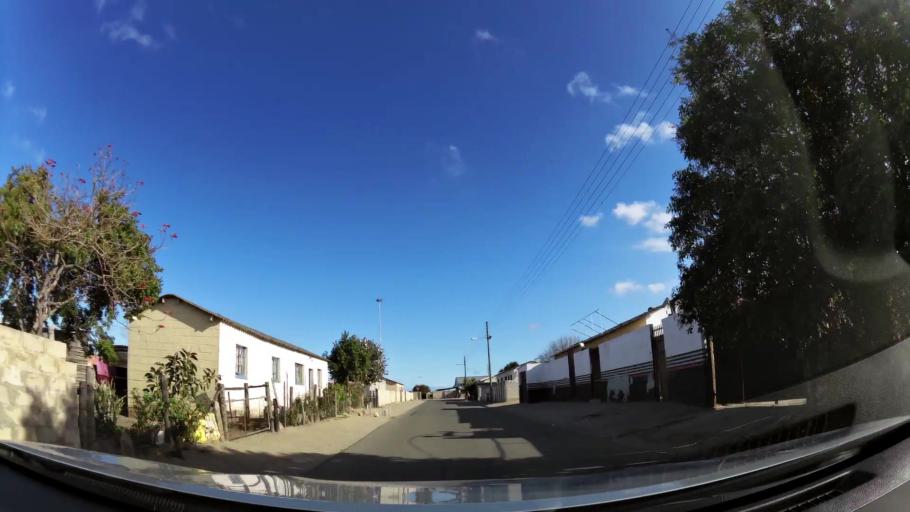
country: ZA
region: Western Cape
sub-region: Eden District Municipality
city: George
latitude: -33.9792
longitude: 22.4809
